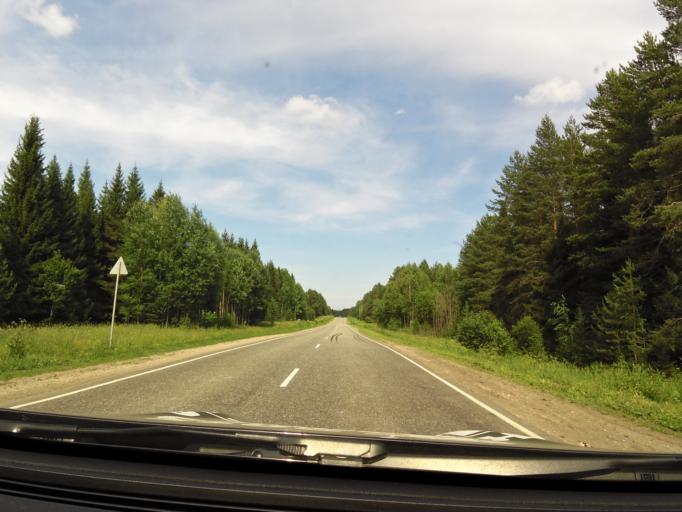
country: RU
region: Kirov
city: Slobodskoy
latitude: 58.7692
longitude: 50.3680
